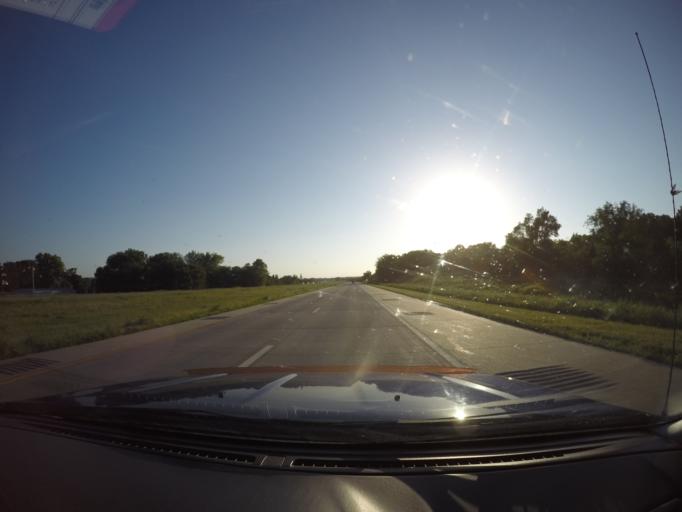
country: US
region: Kansas
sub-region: Riley County
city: Manhattan
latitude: 39.1978
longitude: -96.4765
